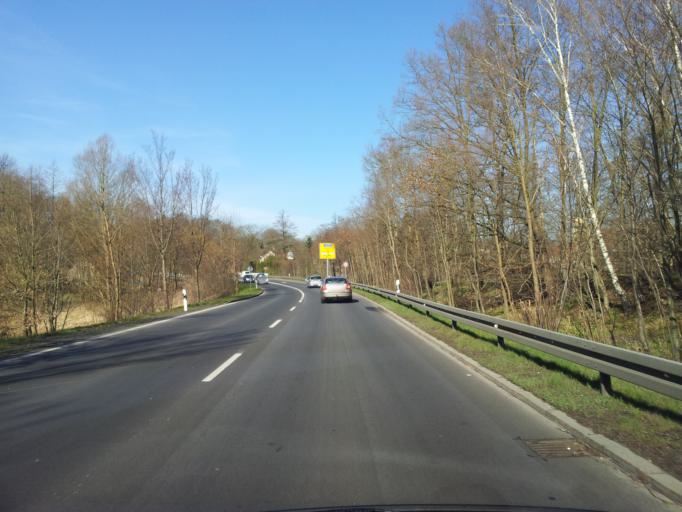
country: DE
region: Saxony
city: Konigsbruck
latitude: 51.2613
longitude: 13.9054
